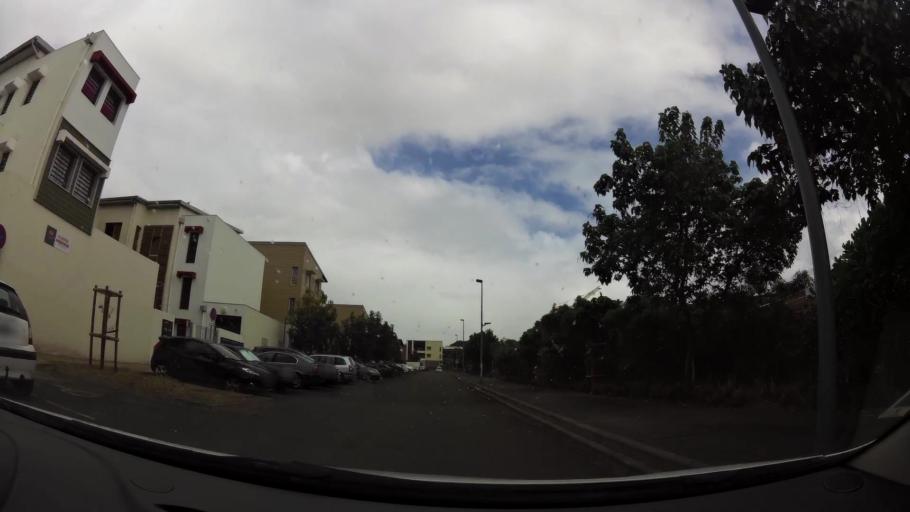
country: RE
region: Reunion
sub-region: Reunion
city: Sainte-Suzanne
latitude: -20.9006
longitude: 55.5977
